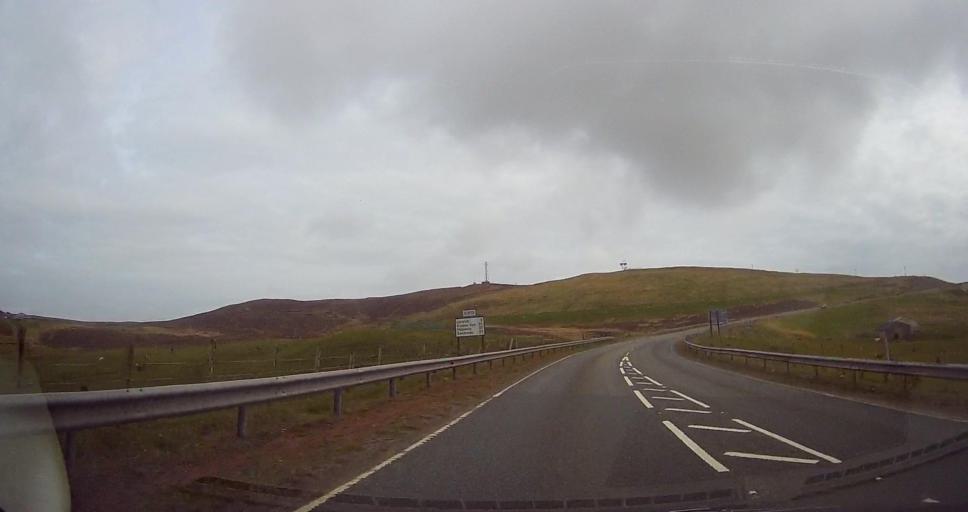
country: GB
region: Scotland
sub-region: Shetland Islands
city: Lerwick
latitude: 60.1374
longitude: -1.2129
